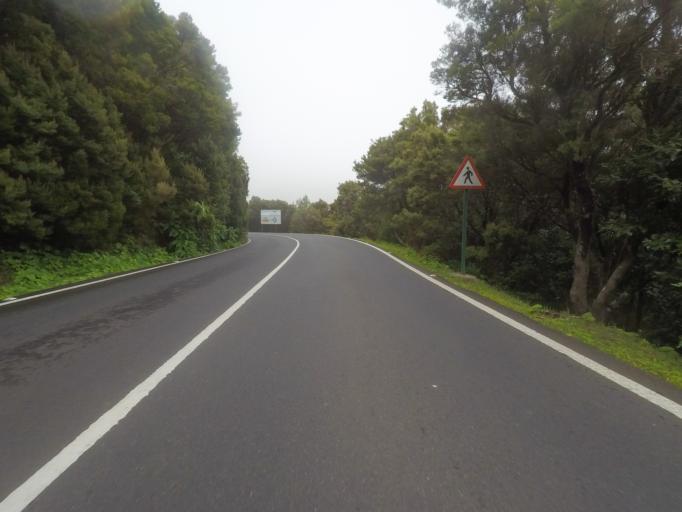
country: ES
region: Canary Islands
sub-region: Provincia de Santa Cruz de Tenerife
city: Alajero
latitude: 28.1082
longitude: -17.2404
